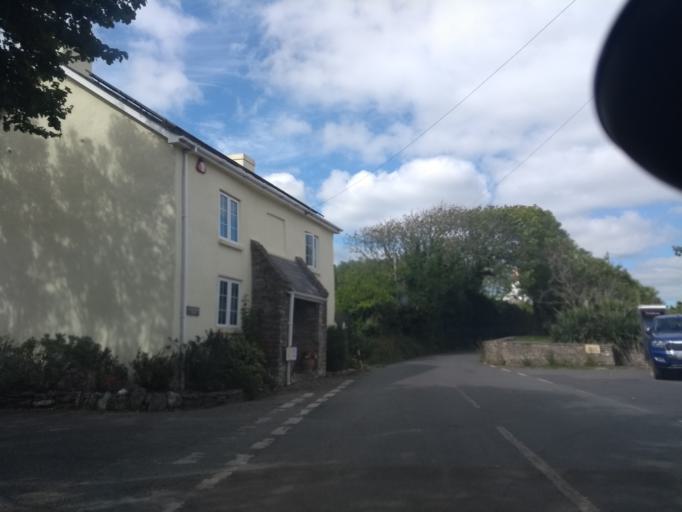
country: GB
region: England
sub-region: Devon
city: Modbury
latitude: 50.2962
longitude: -3.8947
